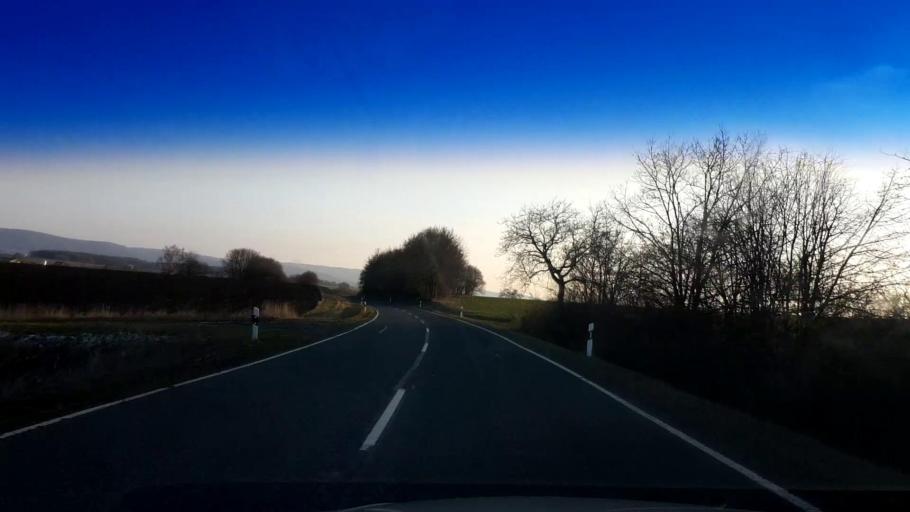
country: DE
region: Bavaria
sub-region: Upper Franconia
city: Schesslitz
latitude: 50.0122
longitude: 11.0108
